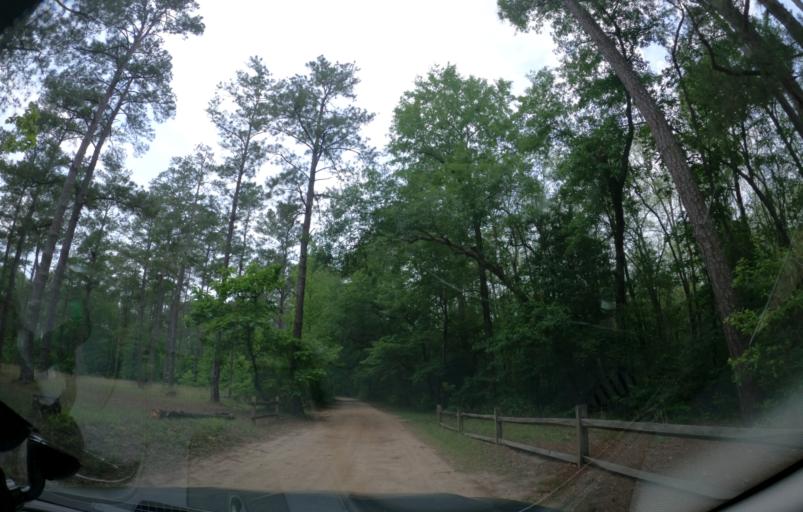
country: US
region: South Carolina
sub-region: Barnwell County
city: Williston
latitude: 33.5520
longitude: -81.4832
